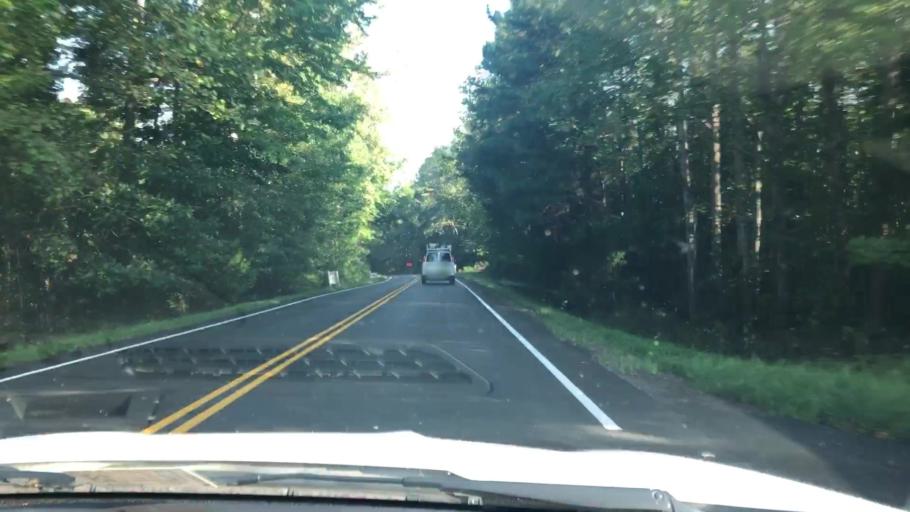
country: US
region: Virginia
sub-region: King William County
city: West Point
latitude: 37.4761
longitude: -76.8464
